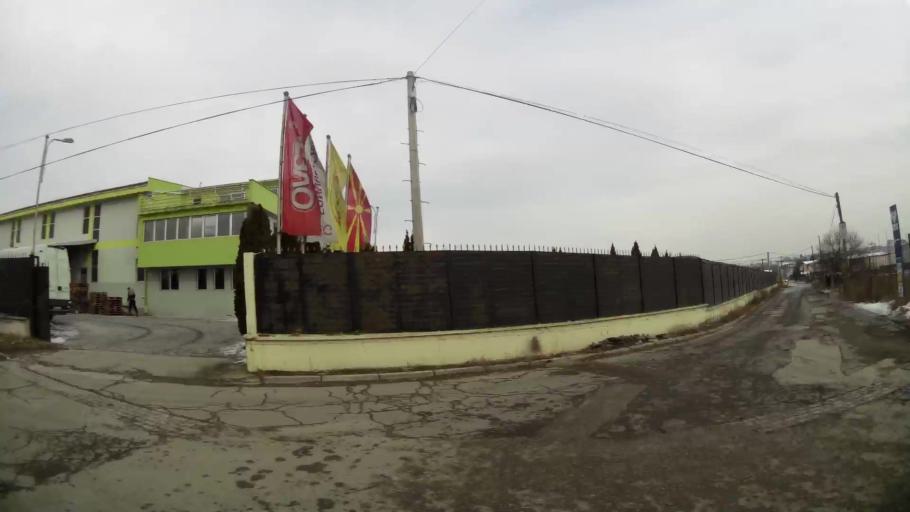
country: MK
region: Suto Orizari
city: Suto Orizare
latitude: 42.0339
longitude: 21.4016
